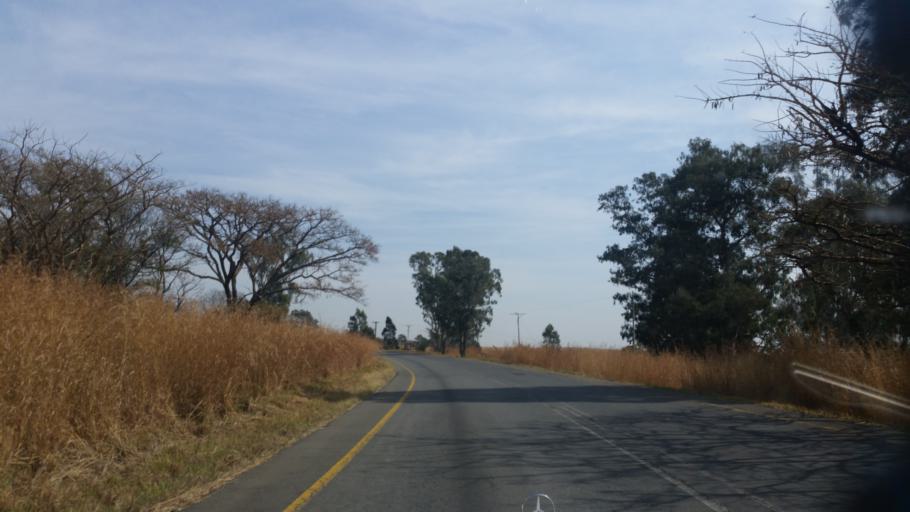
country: ZA
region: KwaZulu-Natal
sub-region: uThukela District Municipality
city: Estcourt
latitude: -29.0696
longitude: 29.9557
